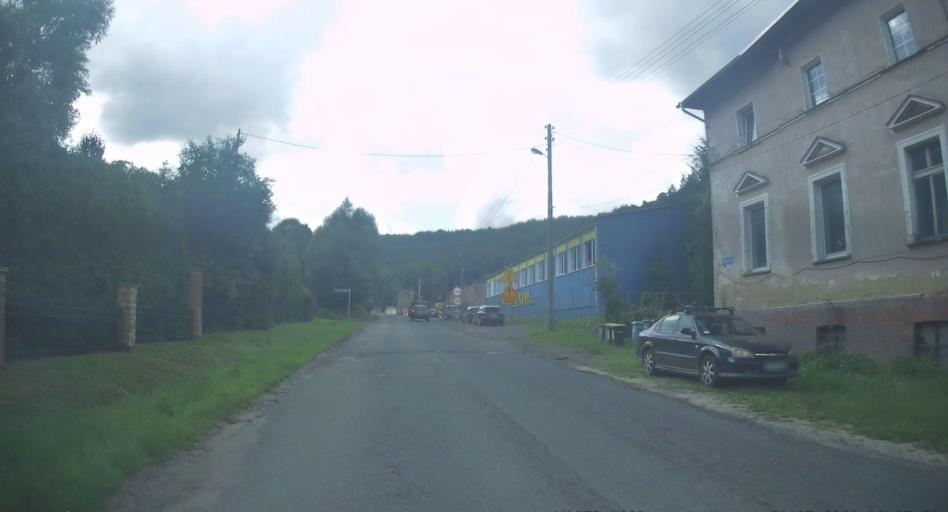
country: PL
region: Lower Silesian Voivodeship
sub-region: Powiat walbrzyski
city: Walim
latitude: 50.7211
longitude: 16.4160
